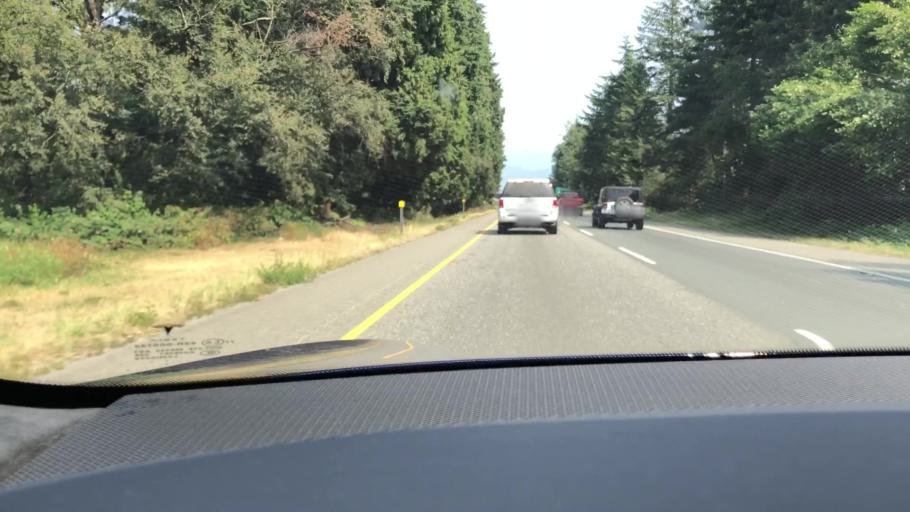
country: US
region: Washington
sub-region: Whatcom County
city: Sumas
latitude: 49.0347
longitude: -122.3048
